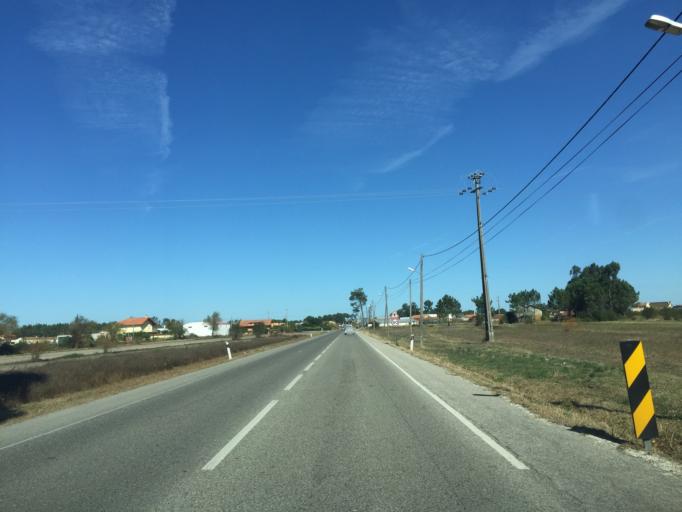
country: PT
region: Coimbra
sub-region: Figueira da Foz
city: Alhadas
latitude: 40.2504
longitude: -8.7849
